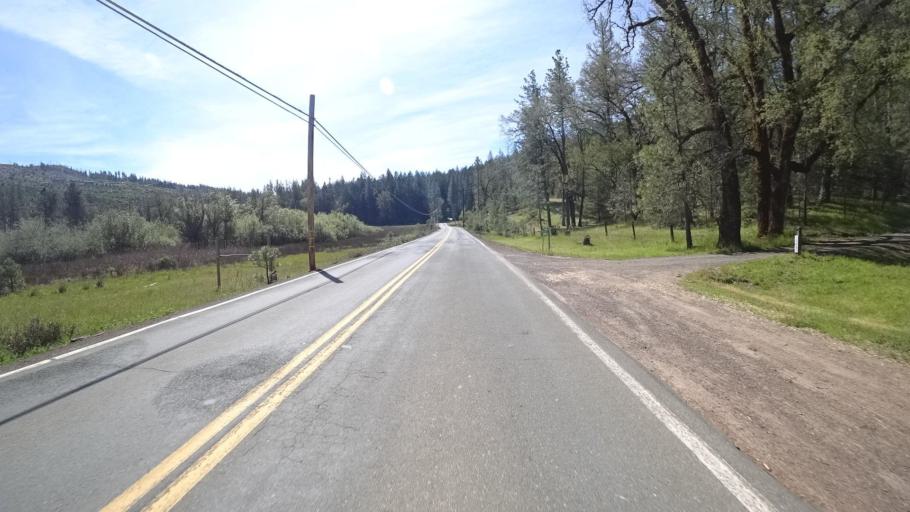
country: US
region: California
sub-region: Lake County
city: Cobb
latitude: 38.8349
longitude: -122.7389
